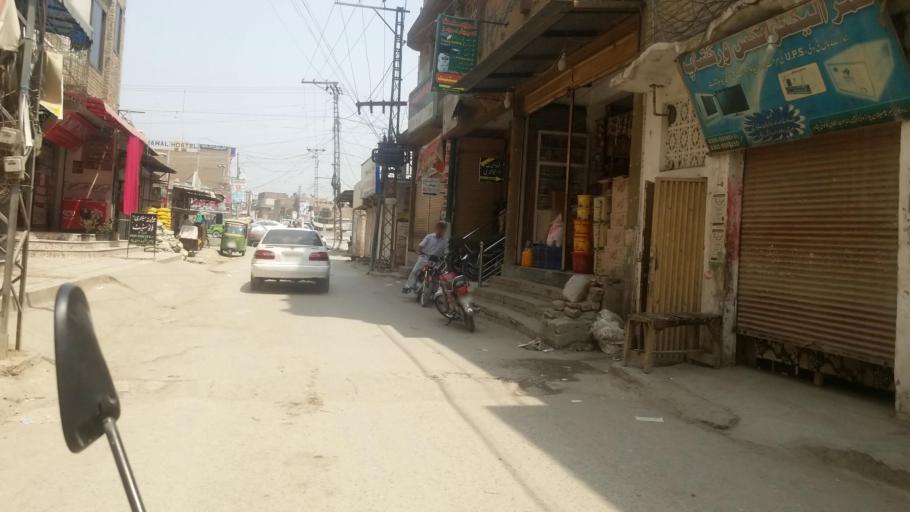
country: PK
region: Khyber Pakhtunkhwa
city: Peshawar
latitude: 34.0317
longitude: 71.5861
